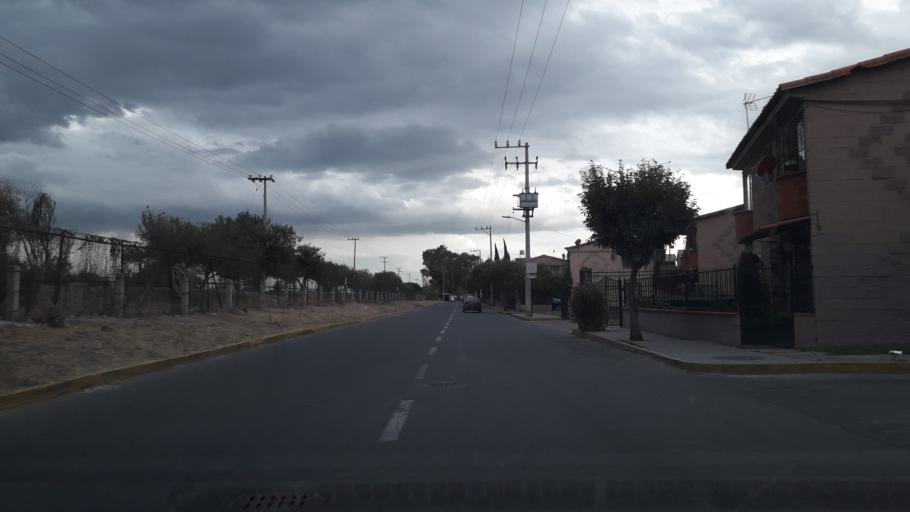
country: MX
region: Mexico
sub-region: Jaltenco
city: Alborada Jaltenco
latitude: 19.6673
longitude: -99.0676
